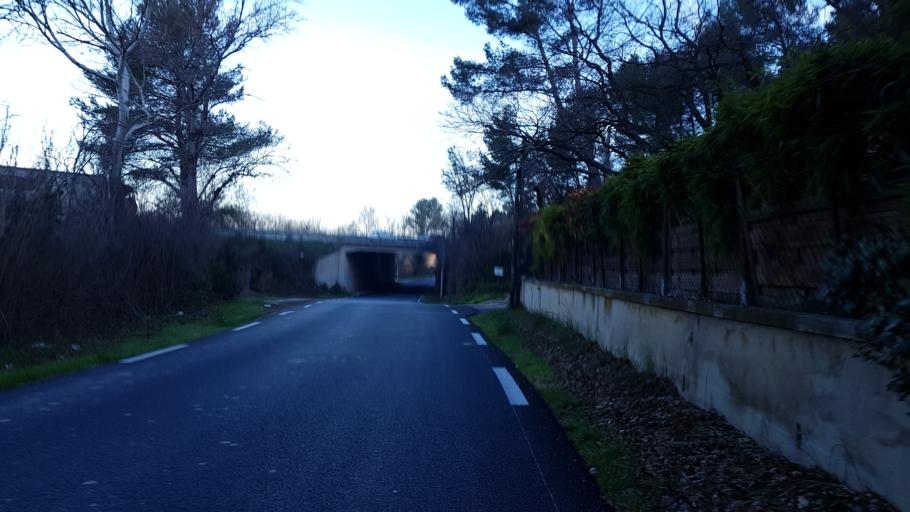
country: FR
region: Provence-Alpes-Cote d'Azur
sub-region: Departement des Bouches-du-Rhone
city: Bouc-Bel-Air
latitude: 43.4979
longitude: 5.4077
